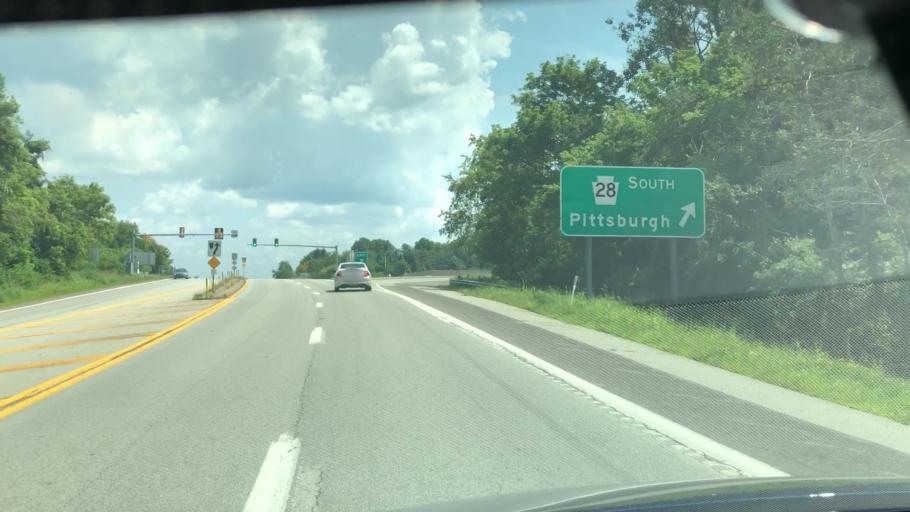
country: US
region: Pennsylvania
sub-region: Armstrong County
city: Freeport
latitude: 40.6922
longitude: -79.7129
